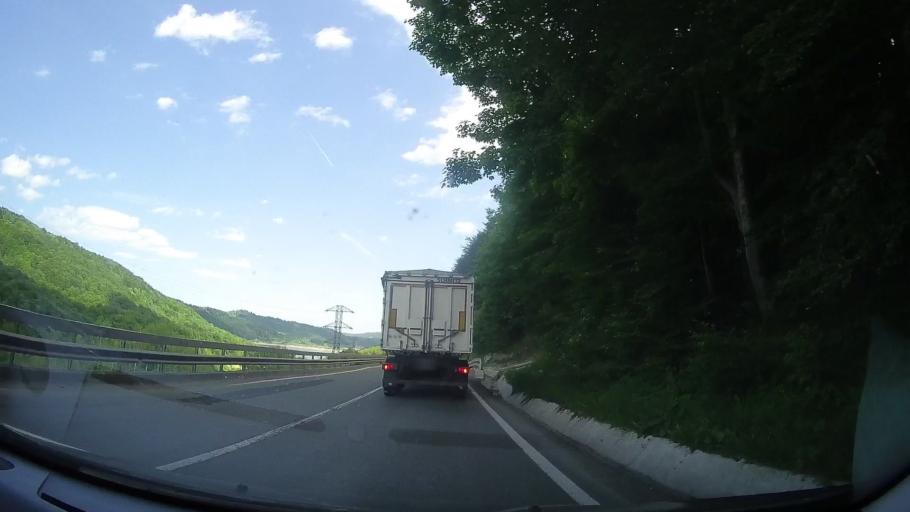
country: RO
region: Prahova
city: Maneciu
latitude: 45.3389
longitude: 25.9587
